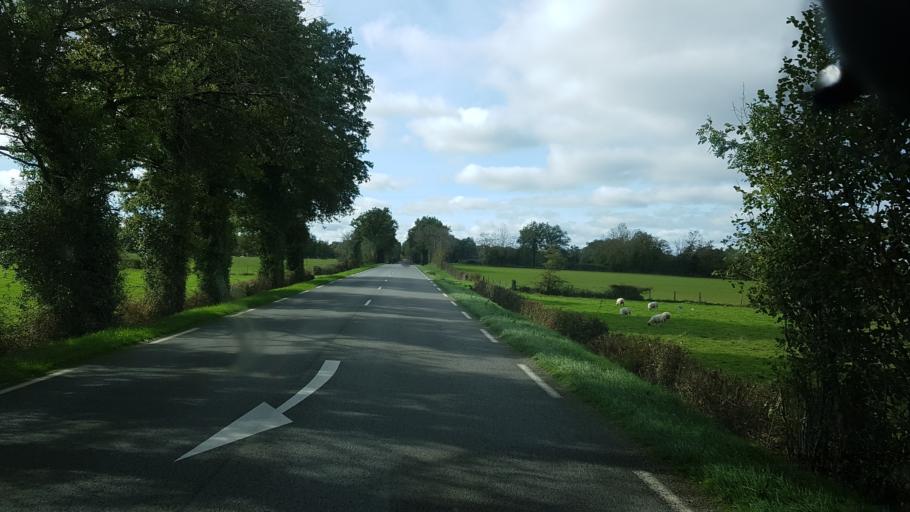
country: FR
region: Poitou-Charentes
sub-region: Departement de la Charente
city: Confolens
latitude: 46.0782
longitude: 0.7871
